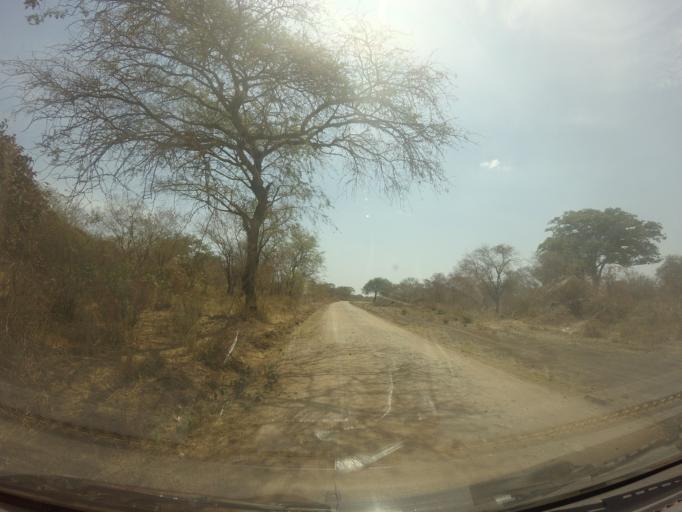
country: UG
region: Northern Region
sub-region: Yumbe District
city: Yumbe
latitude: 3.1896
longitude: 31.2779
